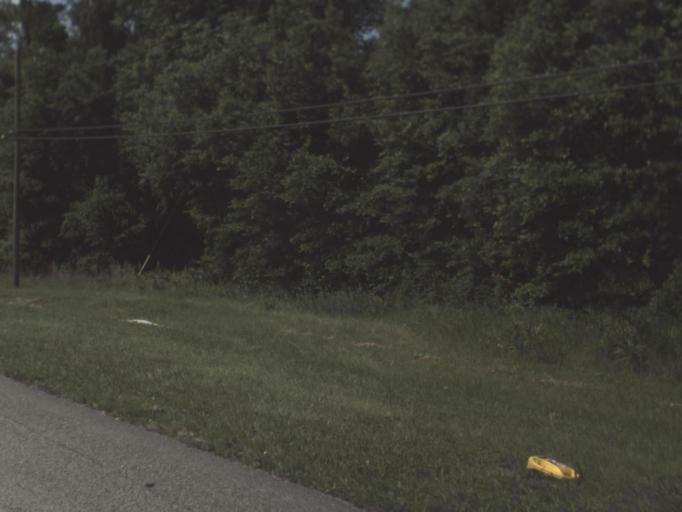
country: US
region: Florida
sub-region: Alachua County
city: Hawthorne
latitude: 29.6183
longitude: -82.0961
